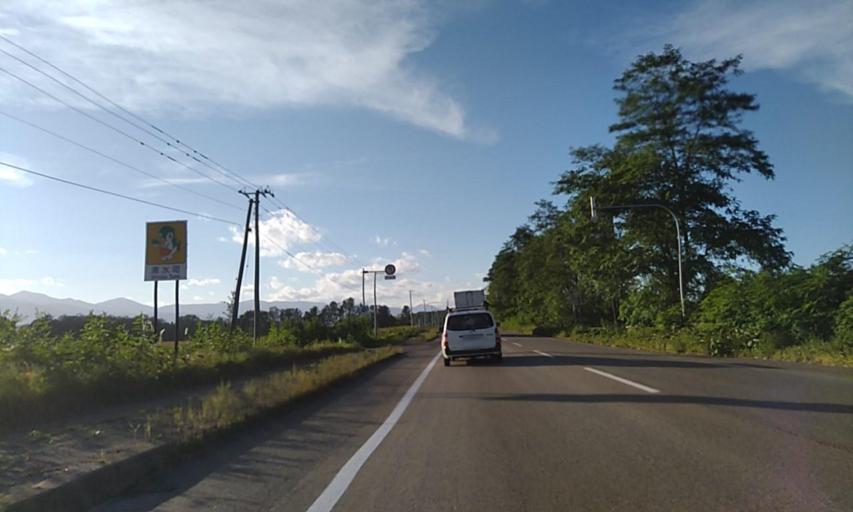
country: JP
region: Hokkaido
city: Obihiro
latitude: 42.9296
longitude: 142.9807
